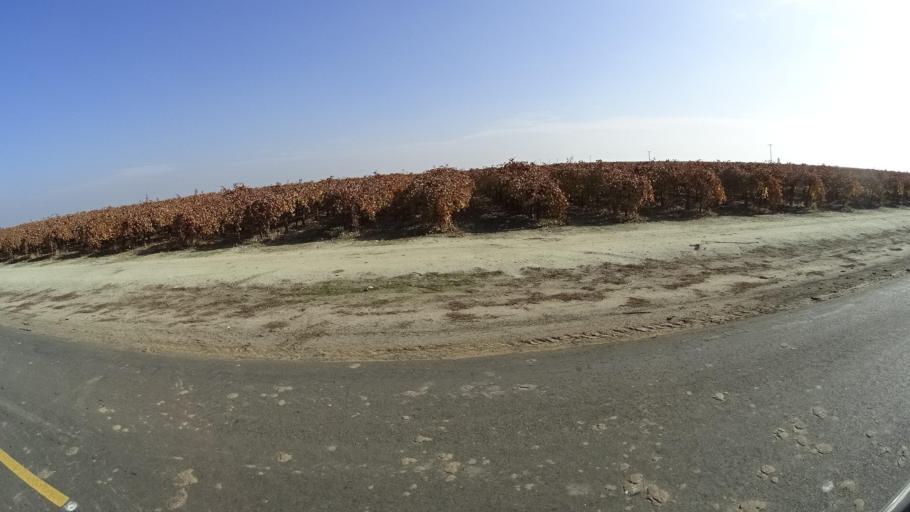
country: US
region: California
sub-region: Kern County
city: McFarland
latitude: 35.6831
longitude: -119.1693
